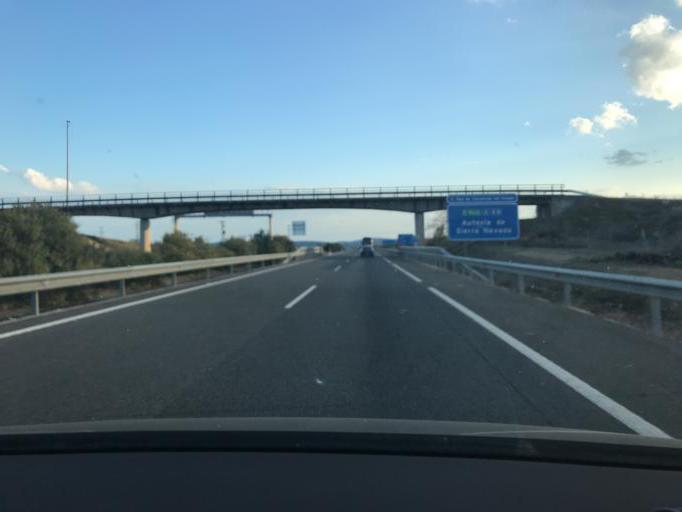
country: ES
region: Andalusia
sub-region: Provincia de Jaen
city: Bailen
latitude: 38.0910
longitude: -3.7386
